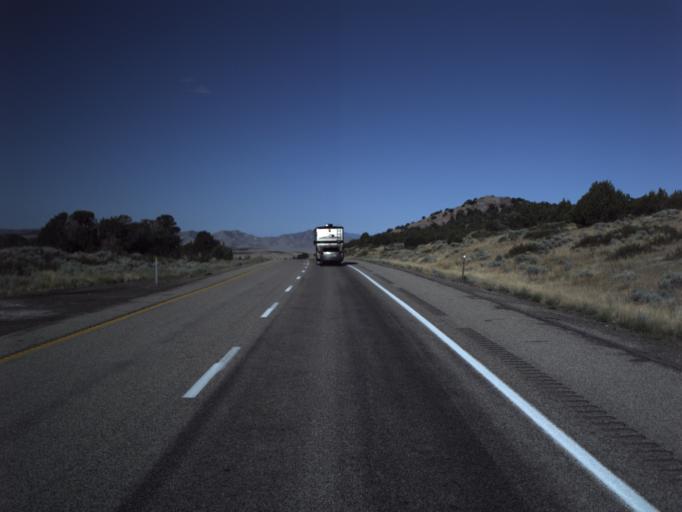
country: US
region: Utah
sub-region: Beaver County
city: Beaver
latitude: 38.6079
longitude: -112.5199
